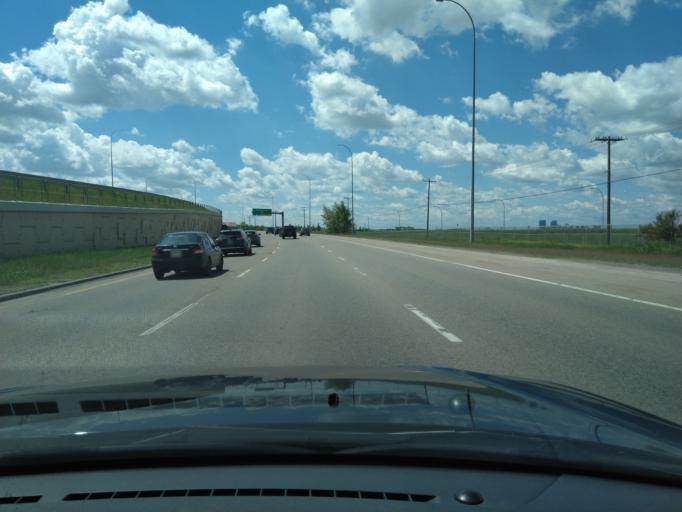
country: CA
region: Alberta
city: Calgary
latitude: 51.1047
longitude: -113.9812
